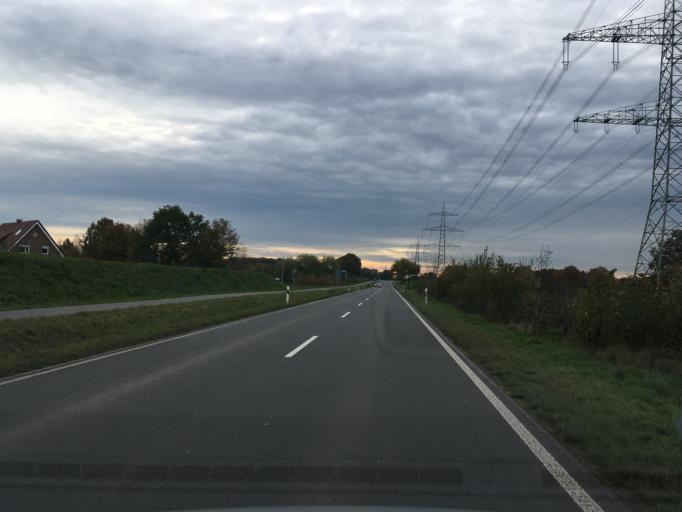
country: DE
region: North Rhine-Westphalia
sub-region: Regierungsbezirk Munster
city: Sudlohn
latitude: 51.8946
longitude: 6.9078
